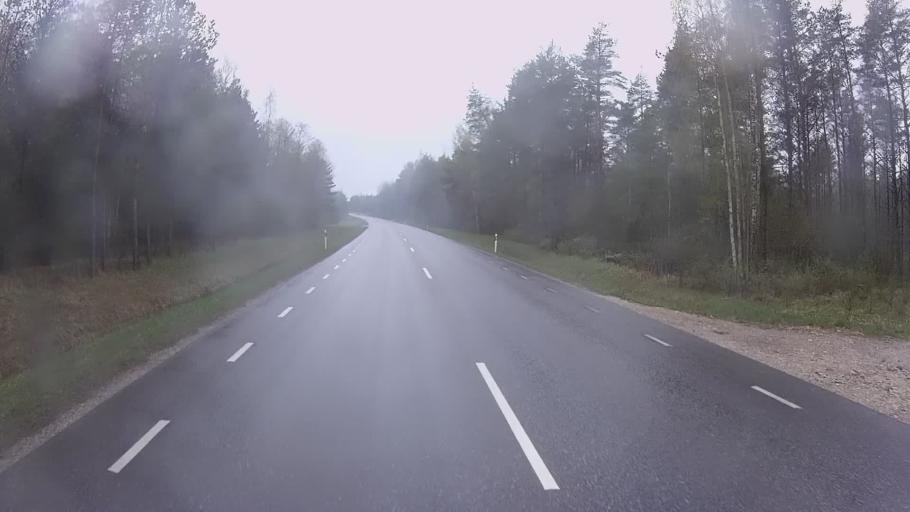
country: EE
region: Hiiumaa
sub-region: Kaerdla linn
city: Kardla
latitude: 58.9871
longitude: 22.5146
